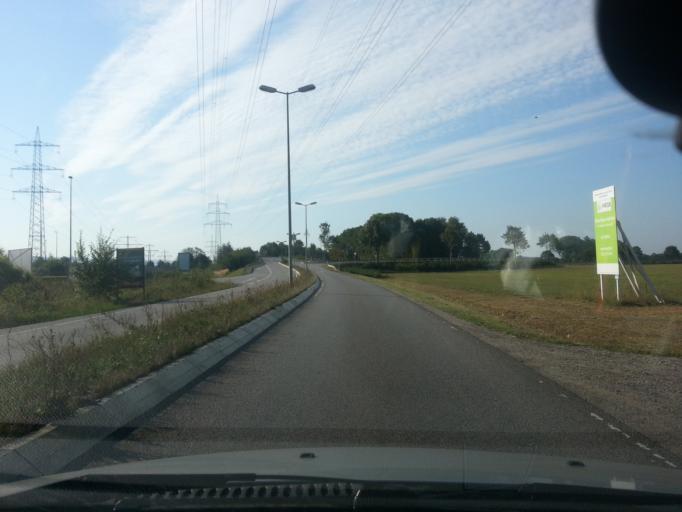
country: DE
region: Hesse
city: Lorsch
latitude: 49.6702
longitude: 8.5836
